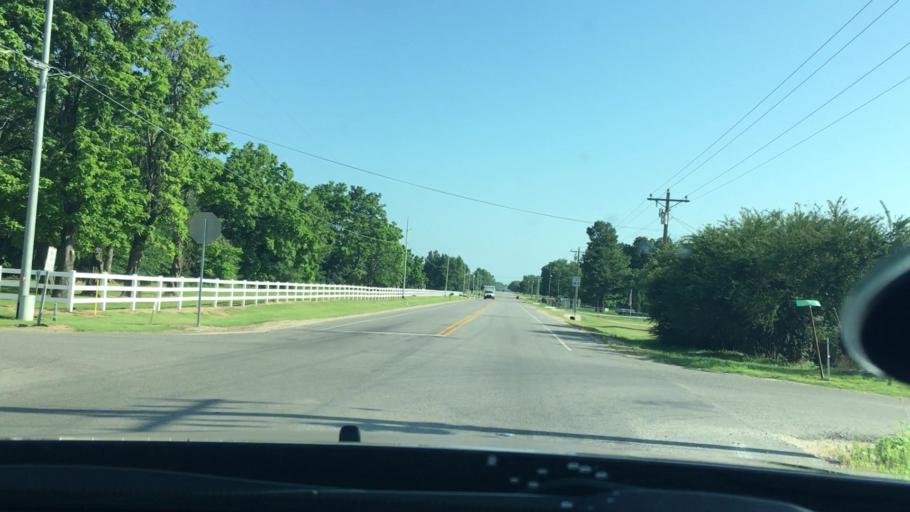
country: US
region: Oklahoma
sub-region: Pontotoc County
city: Ada
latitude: 34.8105
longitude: -96.6522
